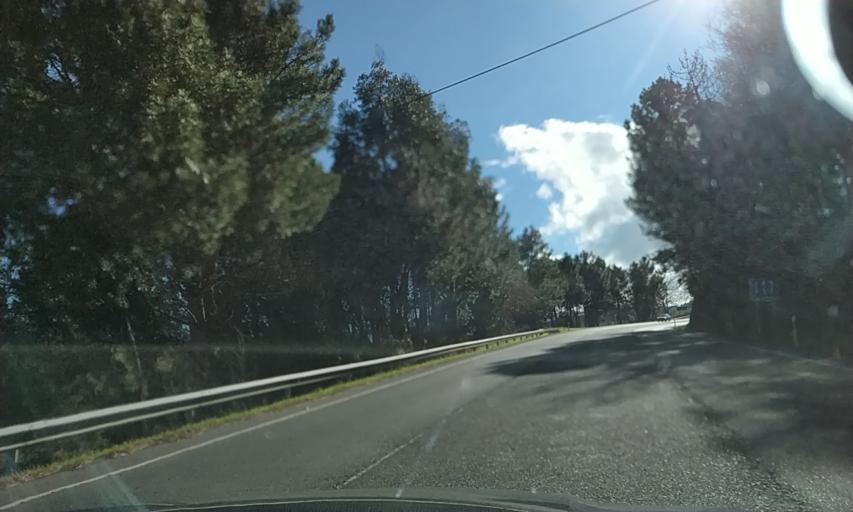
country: ES
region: Galicia
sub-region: Provincia de Pontevedra
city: Silleda
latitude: 42.7033
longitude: -8.3108
